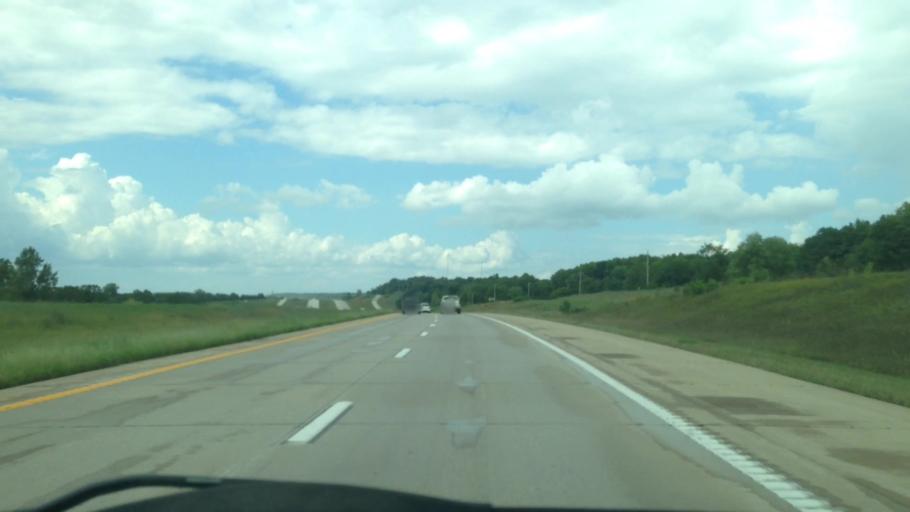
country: US
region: Missouri
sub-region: Pike County
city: Bowling Green
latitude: 39.4247
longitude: -91.2536
